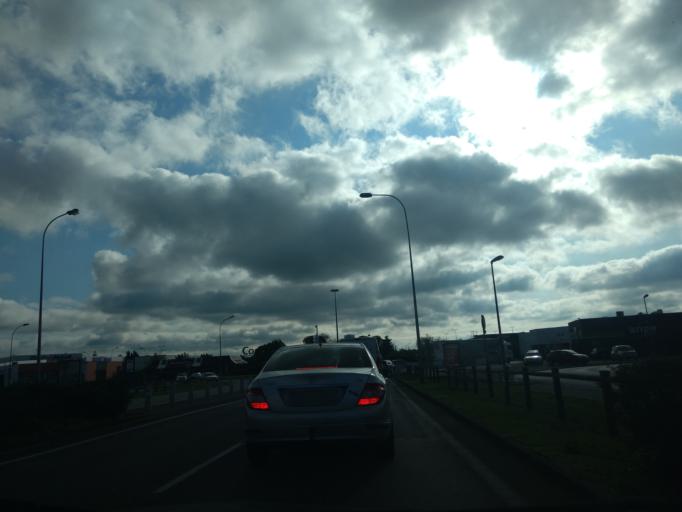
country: FR
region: Poitou-Charentes
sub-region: Departement de la Vienne
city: Chasseneuil-du-Poitou
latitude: 46.6479
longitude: 0.3627
